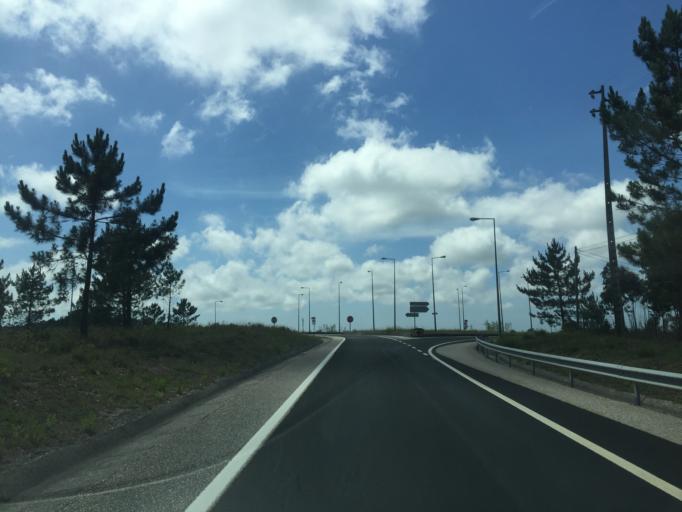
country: PT
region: Leiria
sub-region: Marinha Grande
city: Marinha Grande
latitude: 39.7155
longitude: -8.9231
